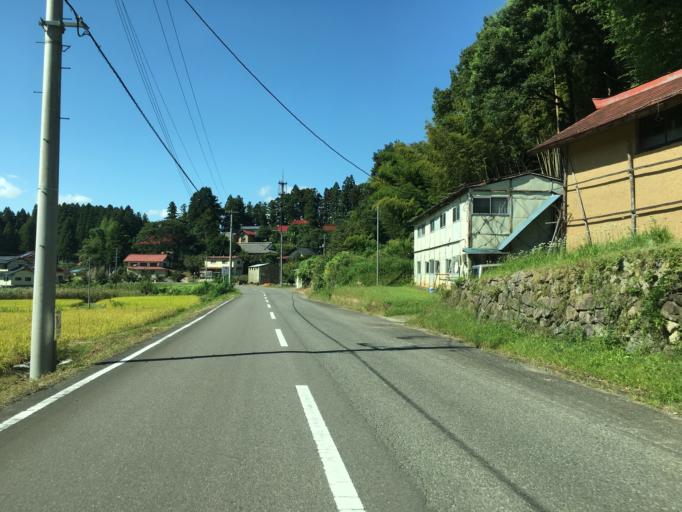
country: JP
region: Fukushima
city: Sukagawa
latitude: 37.2798
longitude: 140.4576
